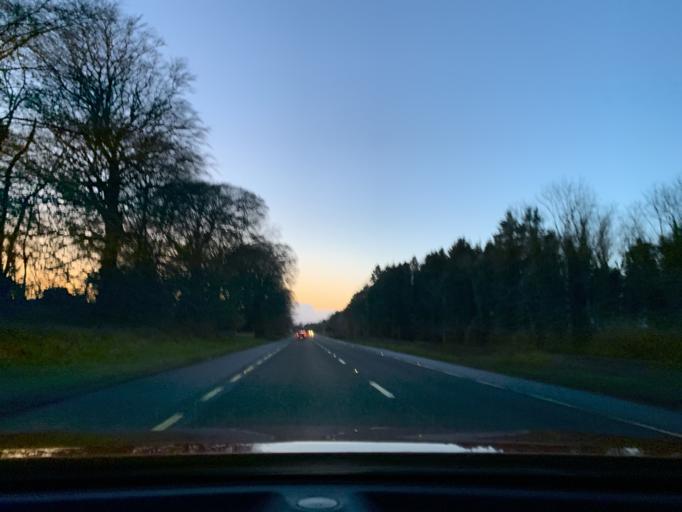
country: IE
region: Connaught
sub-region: Roscommon
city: Boyle
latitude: 53.9691
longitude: -8.2299
